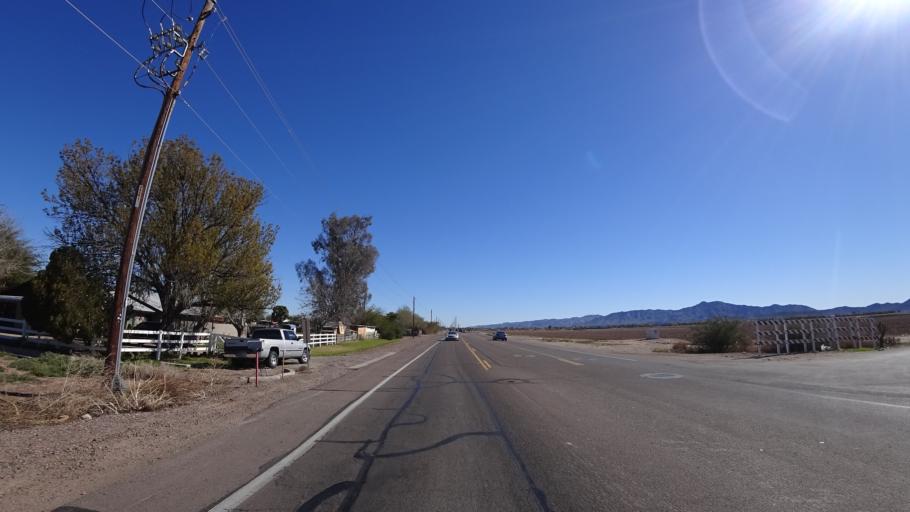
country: US
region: Arizona
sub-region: Maricopa County
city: Laveen
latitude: 33.3774
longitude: -112.1947
